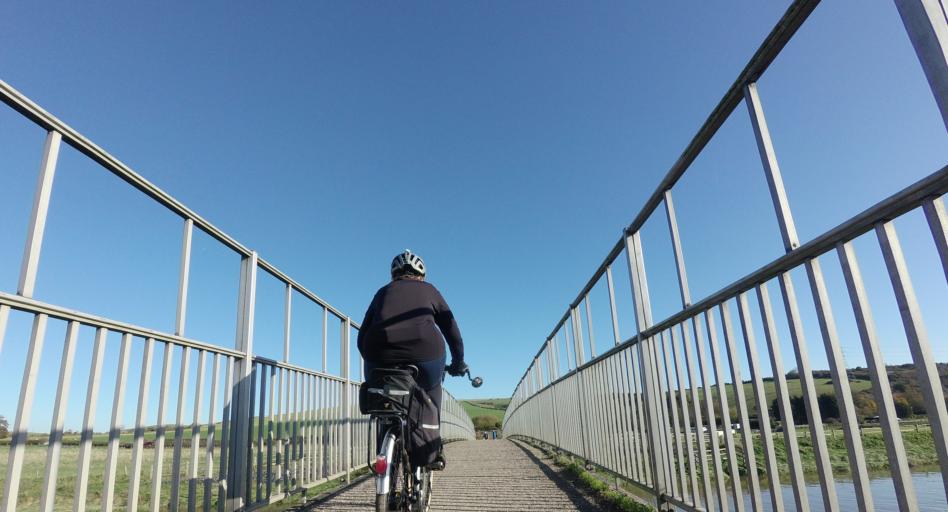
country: GB
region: England
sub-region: West Sussex
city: Steyning
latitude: 50.8707
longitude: -0.3011
